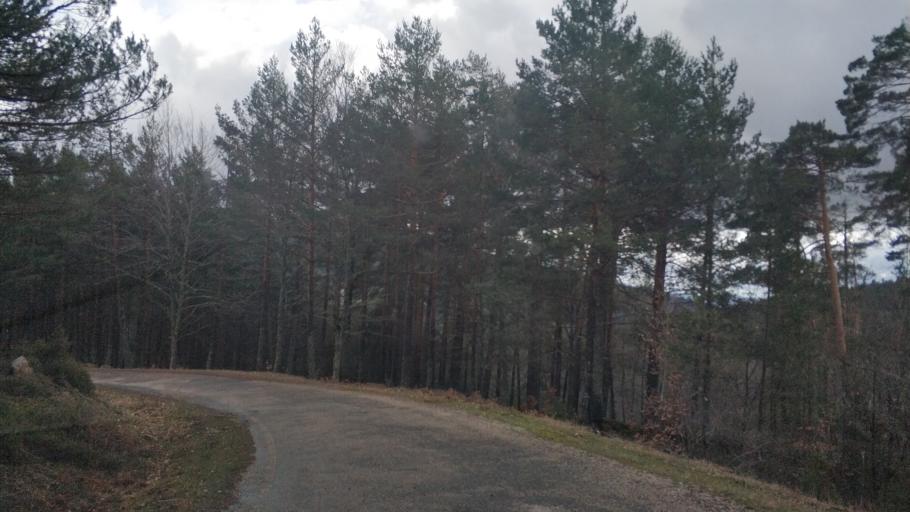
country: ES
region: Castille and Leon
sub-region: Provincia de Burgos
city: Neila
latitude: 42.0436
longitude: -3.0162
